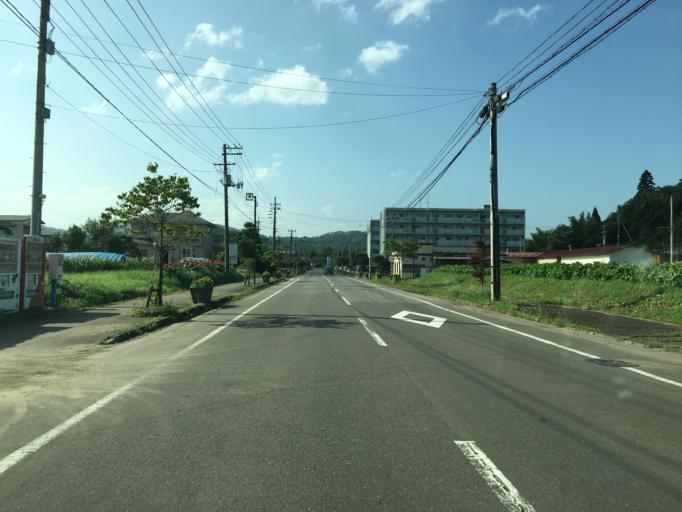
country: JP
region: Miyagi
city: Marumori
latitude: 37.9279
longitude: 140.7637
